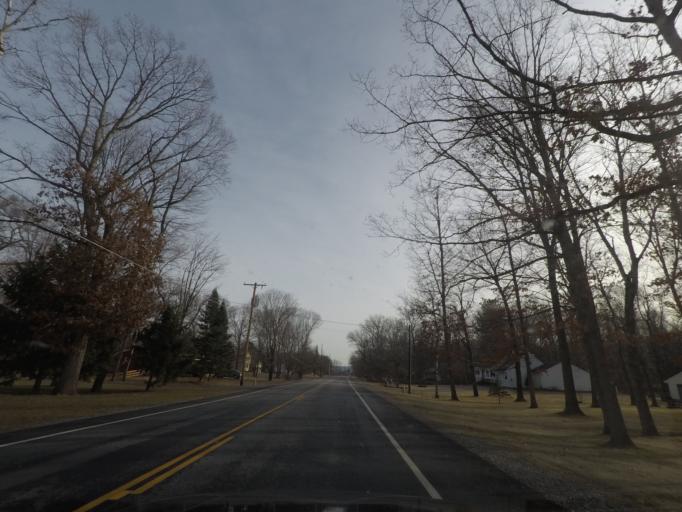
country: US
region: New York
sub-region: Saratoga County
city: Mechanicville
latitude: 42.8639
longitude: -73.6964
